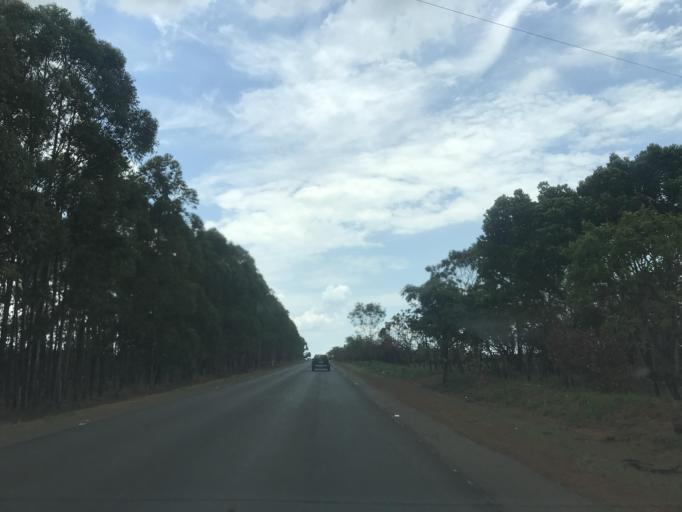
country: BR
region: Goias
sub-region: Vianopolis
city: Vianopolis
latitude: -16.9362
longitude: -48.5573
